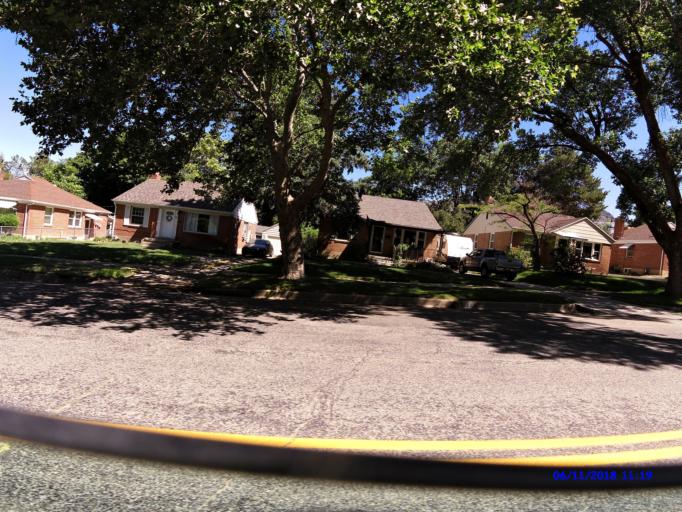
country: US
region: Utah
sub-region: Weber County
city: Ogden
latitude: 41.2224
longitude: -111.9420
